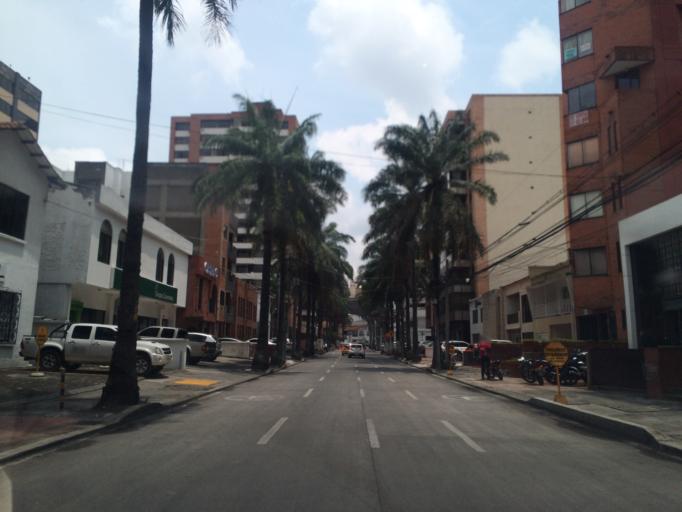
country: CO
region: Valle del Cauca
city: Cali
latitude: 3.4635
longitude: -76.5292
